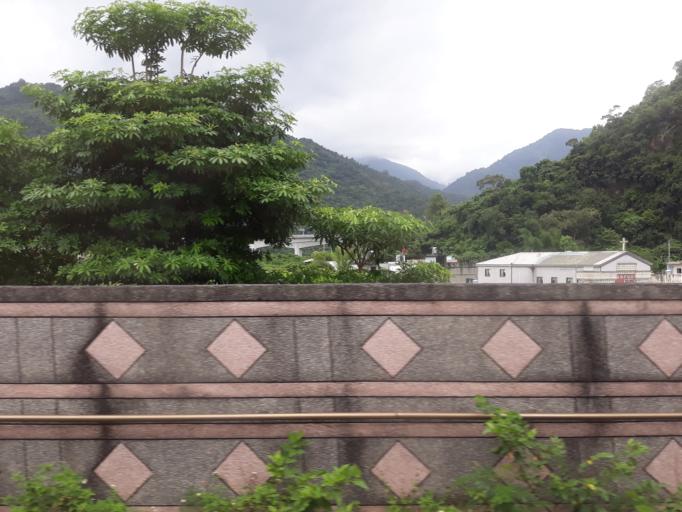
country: TW
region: Taiwan
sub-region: Yilan
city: Yilan
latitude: 24.4441
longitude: 121.7780
